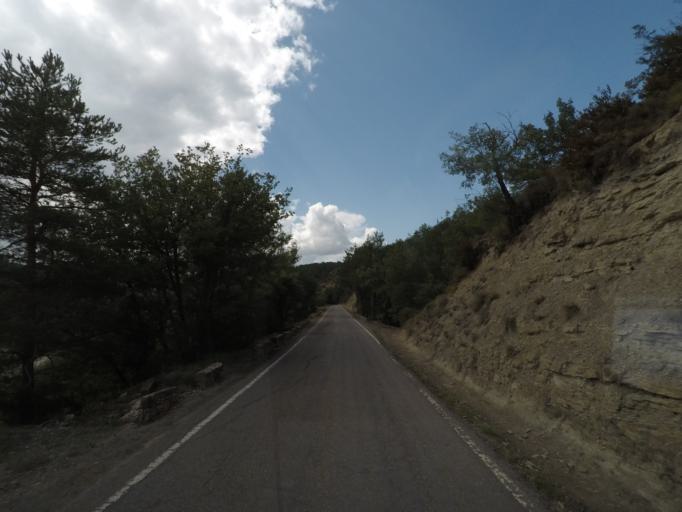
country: ES
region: Aragon
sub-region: Provincia de Huesca
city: Yebra de Basa
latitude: 42.4008
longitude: -0.2563
